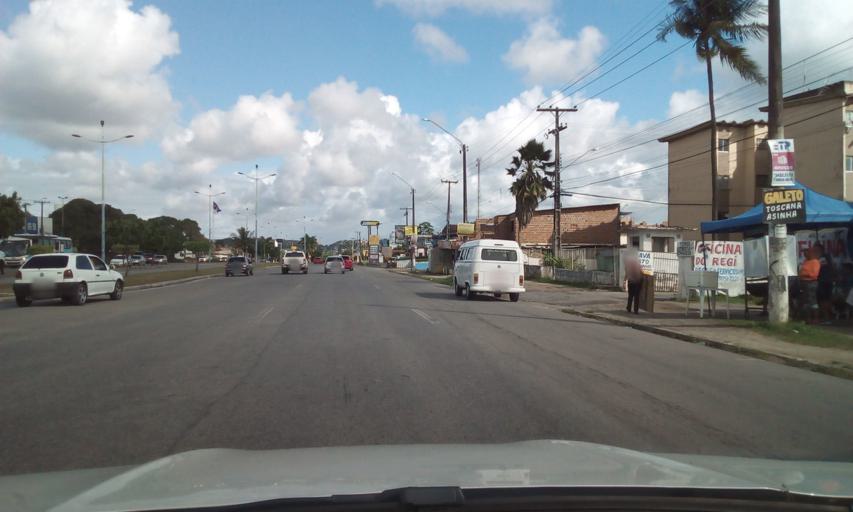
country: BR
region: Pernambuco
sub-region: Abreu E Lima
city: Abreu e Lima
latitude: -7.8753
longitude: -34.9060
